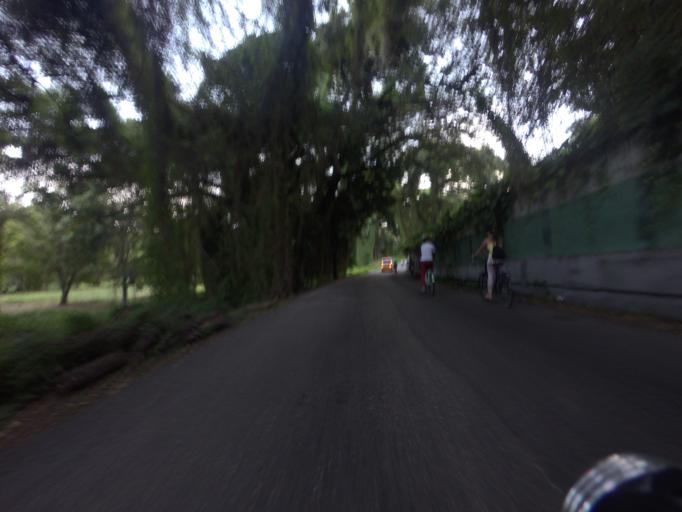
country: CU
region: La Habana
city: Cerro
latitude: 23.1123
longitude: -82.4067
